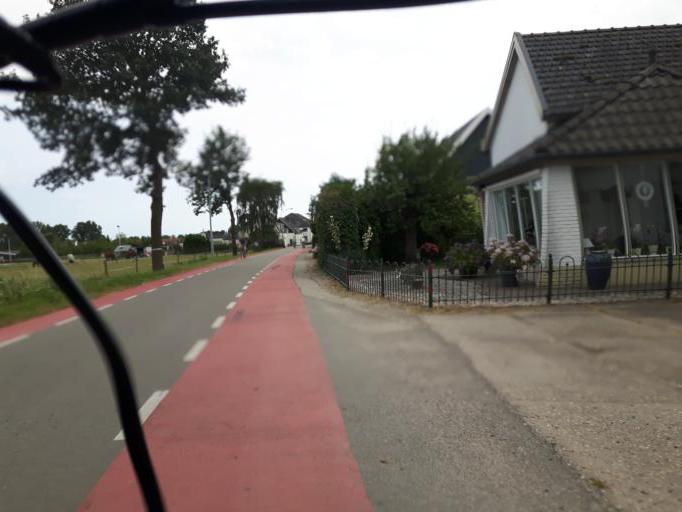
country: NL
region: Gelderland
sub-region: Gemeente Tiel
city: Tiel
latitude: 51.8779
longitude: 5.3737
